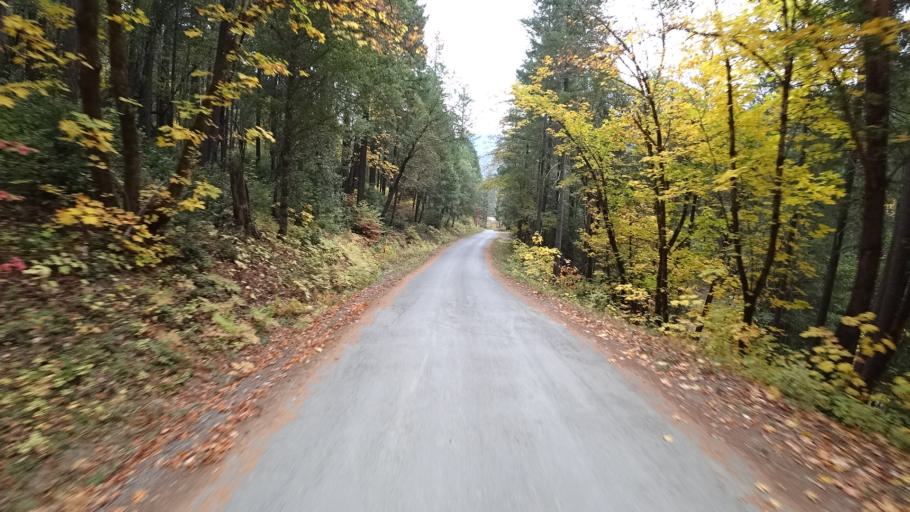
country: US
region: California
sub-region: Siskiyou County
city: Happy Camp
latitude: 41.8239
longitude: -123.3843
